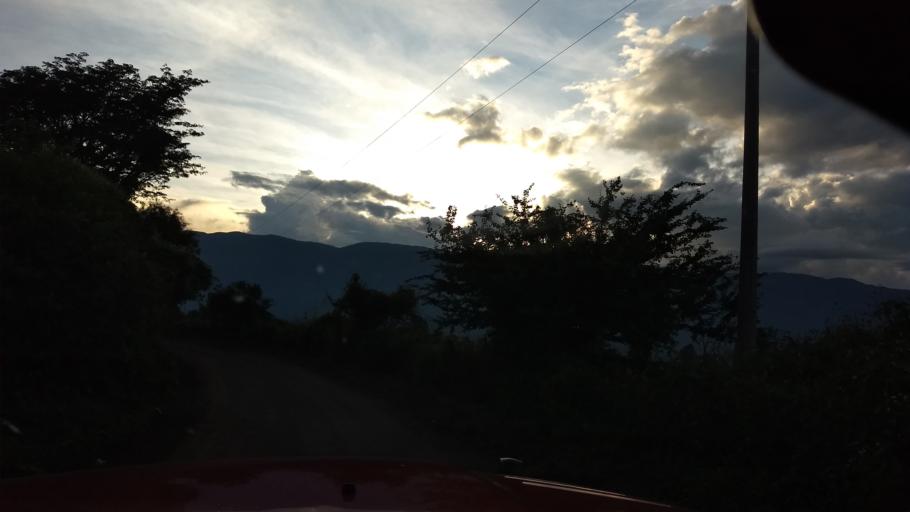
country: MX
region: Colima
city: Suchitlan
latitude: 19.4866
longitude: -103.7922
